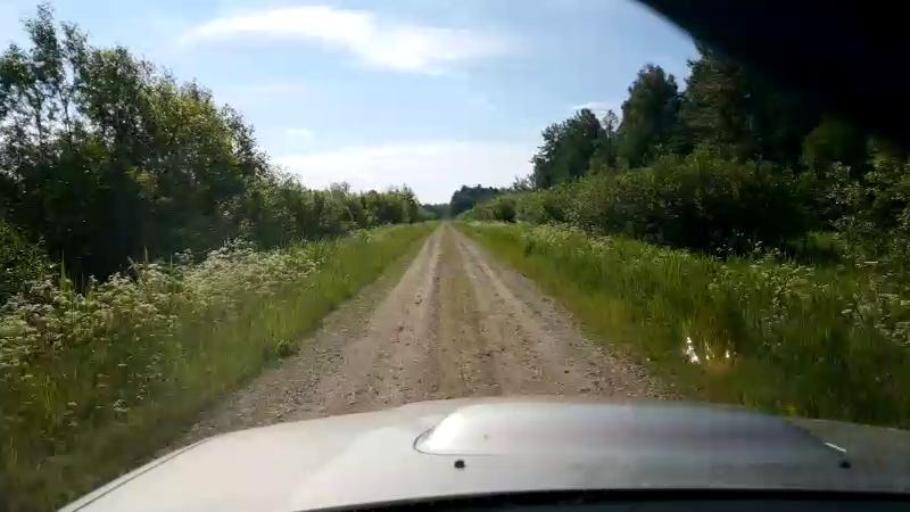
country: EE
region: Paernumaa
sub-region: Sindi linn
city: Sindi
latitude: 58.4947
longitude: 24.6631
